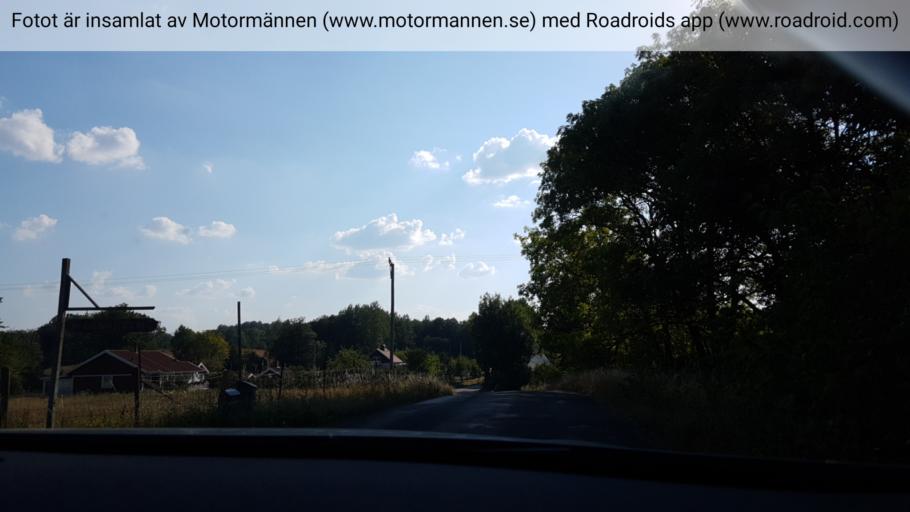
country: SE
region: Vaestra Goetaland
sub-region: Skovde Kommun
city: Stopen
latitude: 58.4839
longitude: 13.7586
